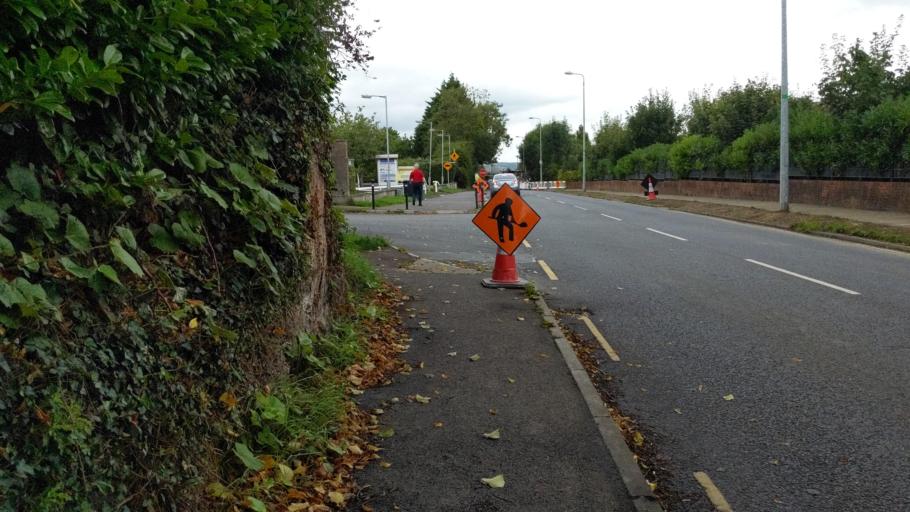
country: IE
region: Leinster
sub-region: Lu
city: Drogheda
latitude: 53.7038
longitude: -6.3479
